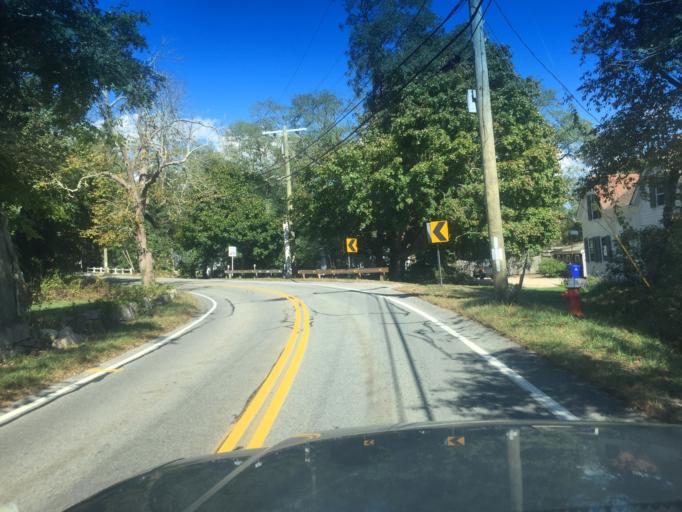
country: US
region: Massachusetts
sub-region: Barnstable County
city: Pocasset
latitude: 41.6665
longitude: -70.6066
